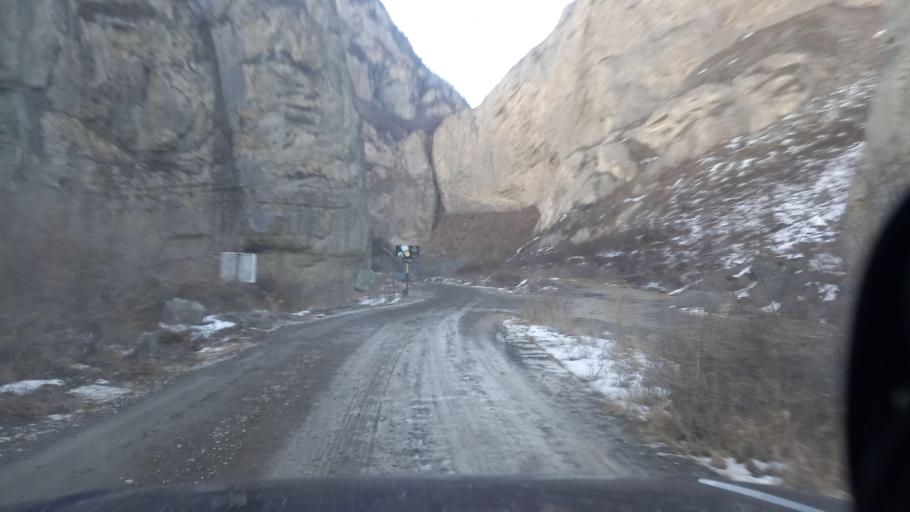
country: RU
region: Ingushetiya
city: Dzhayrakh
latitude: 42.8632
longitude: 44.5196
